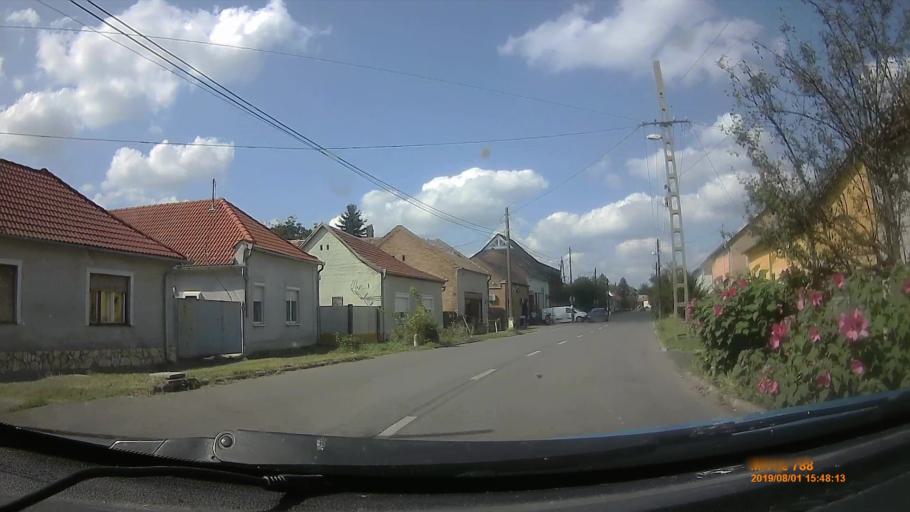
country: HU
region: Baranya
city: Szentlorinc
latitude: 46.0363
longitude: 17.9849
